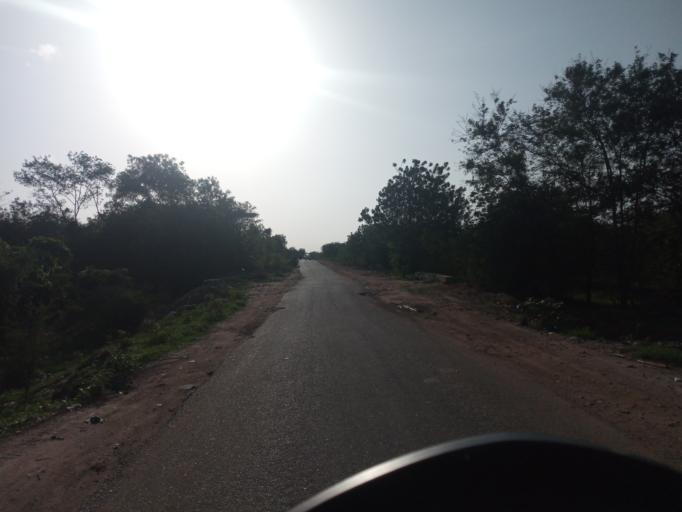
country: IN
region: Telangana
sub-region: Rangareddi
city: Quthbullapur
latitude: 17.5535
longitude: 78.4174
